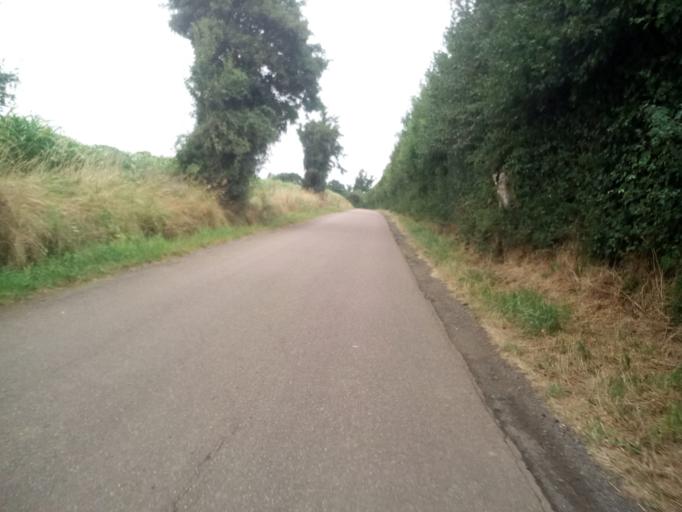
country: FR
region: Lower Normandy
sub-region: Departement du Calvados
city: Clinchamps-sur-Orne
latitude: 49.0382
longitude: -0.3934
